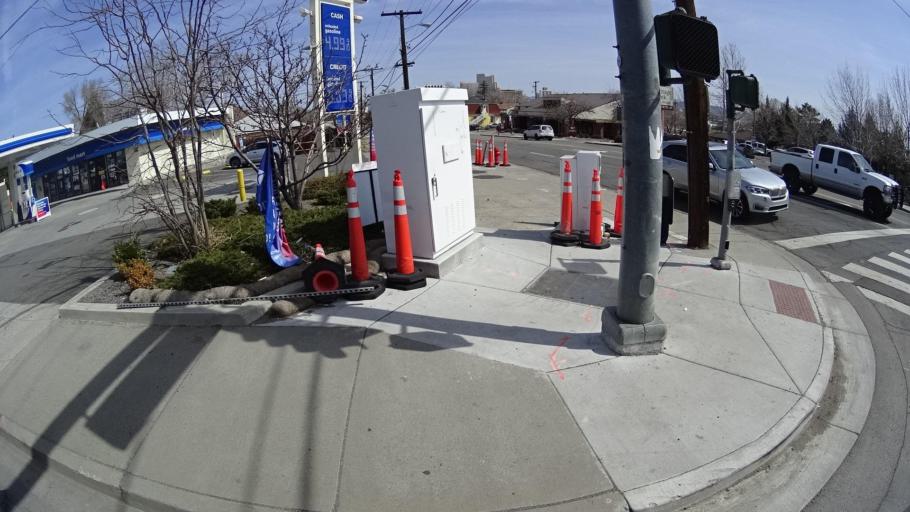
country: US
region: Nevada
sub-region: Washoe County
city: Reno
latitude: 39.5310
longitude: -119.8312
